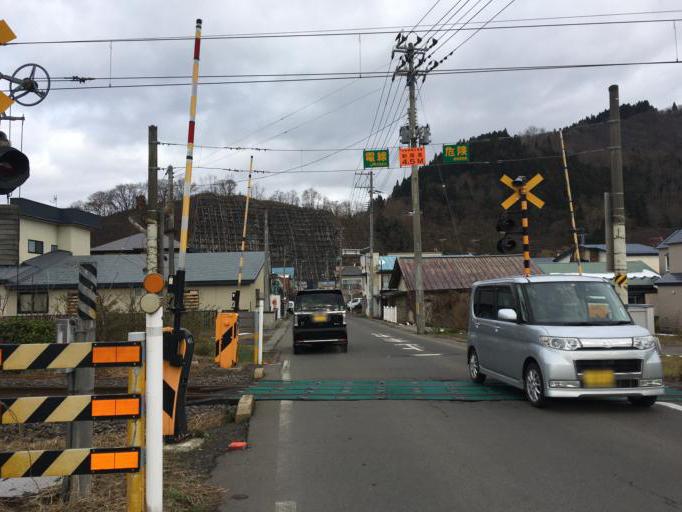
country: JP
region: Aomori
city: Hirosaki
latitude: 40.5211
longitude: 140.5640
